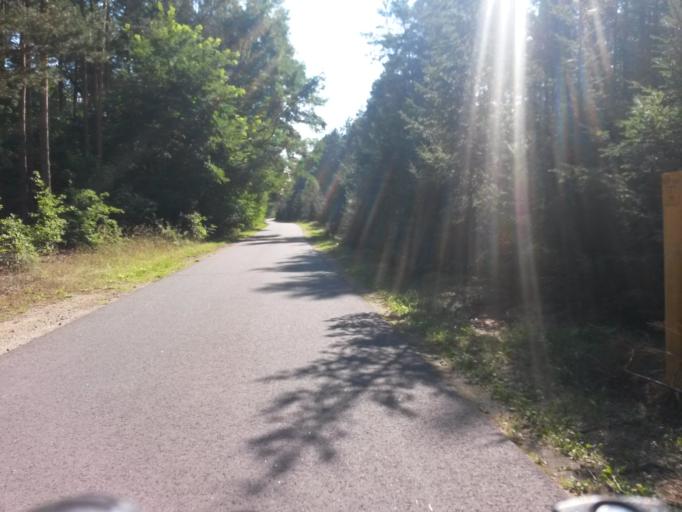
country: DE
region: Brandenburg
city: Templin
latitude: 53.0473
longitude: 13.4828
